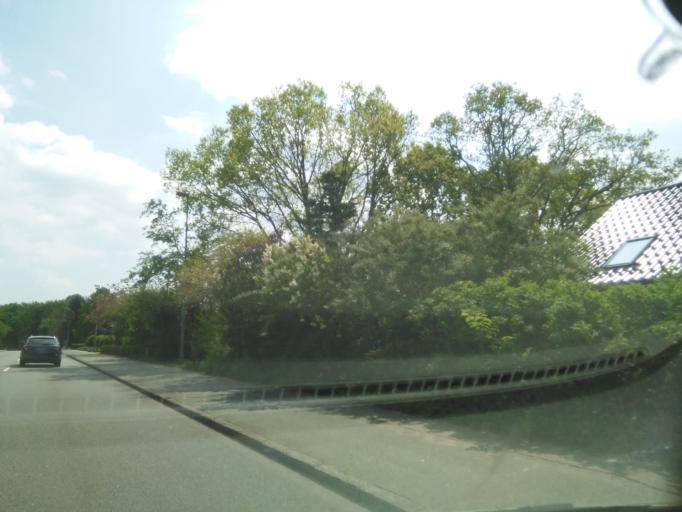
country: DK
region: Central Jutland
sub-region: Skanderborg Kommune
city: Skanderborg
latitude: 56.0358
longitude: 9.9484
